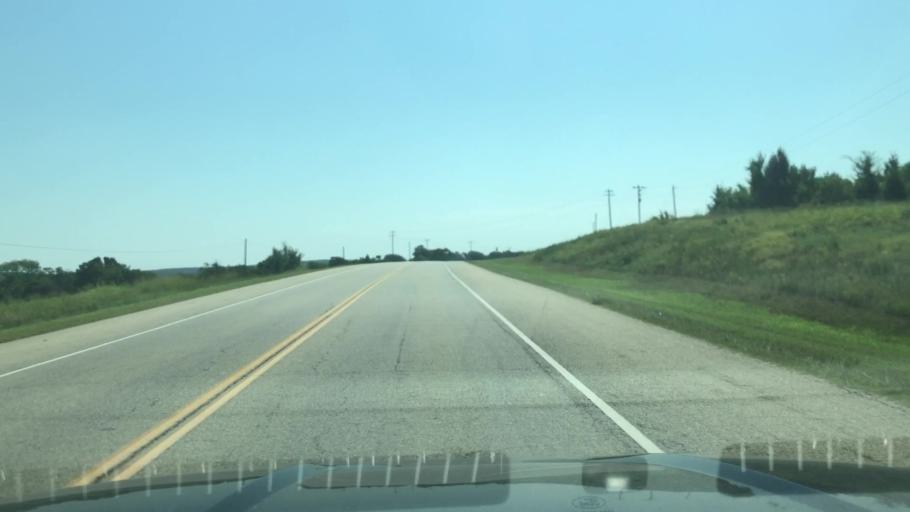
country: US
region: Oklahoma
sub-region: Creek County
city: Kellyville
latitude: 35.9885
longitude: -96.3384
